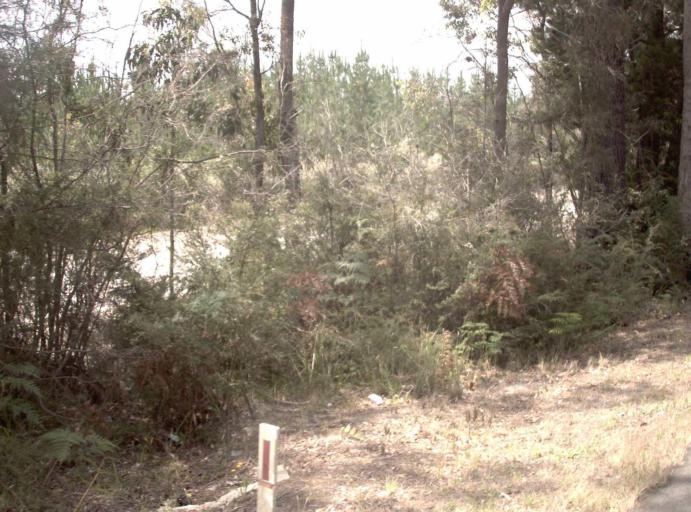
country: AU
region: Victoria
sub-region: Latrobe
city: Traralgon
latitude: -38.2749
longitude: 146.6924
